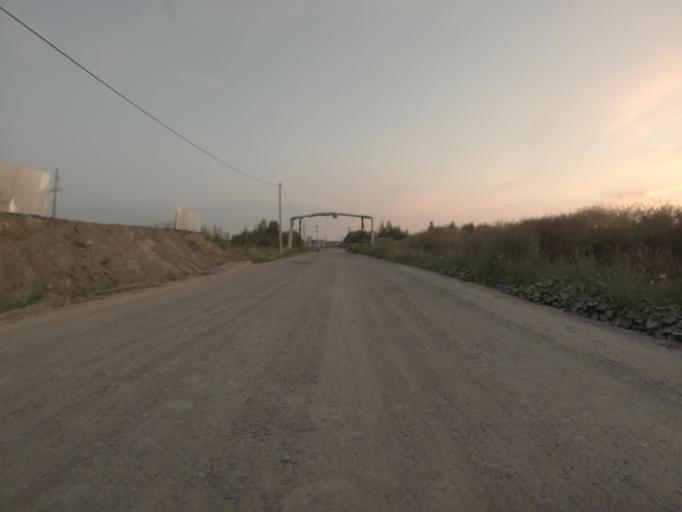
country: RU
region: Leningrad
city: Yanino Vtoroye
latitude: 59.9358
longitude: 30.5949
